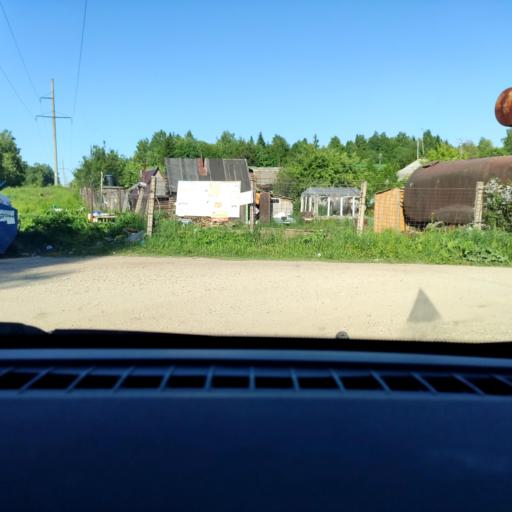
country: RU
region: Perm
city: Overyata
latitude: 58.1235
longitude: 55.8758
